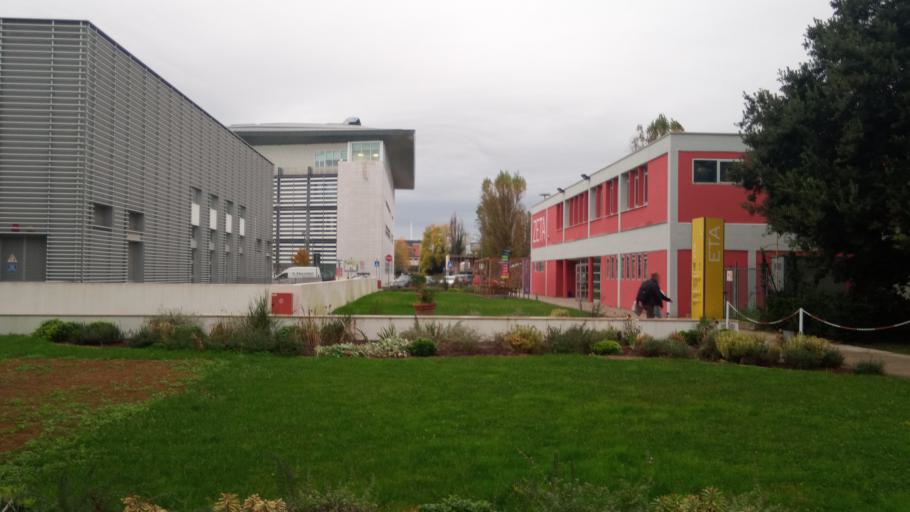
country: IT
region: Veneto
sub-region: Provincia di Venezia
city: Mestre
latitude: 45.4783
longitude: 12.2561
